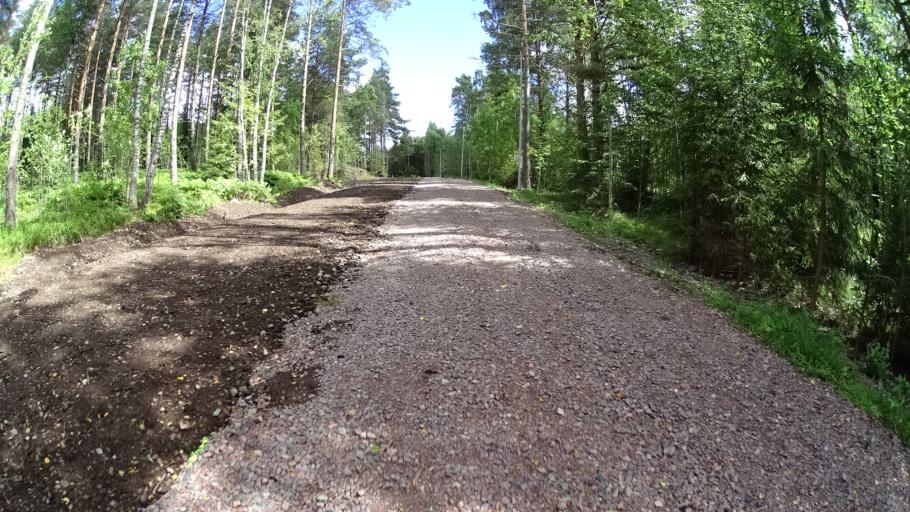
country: FI
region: Uusimaa
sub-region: Helsinki
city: Espoo
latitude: 60.1832
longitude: 24.6885
